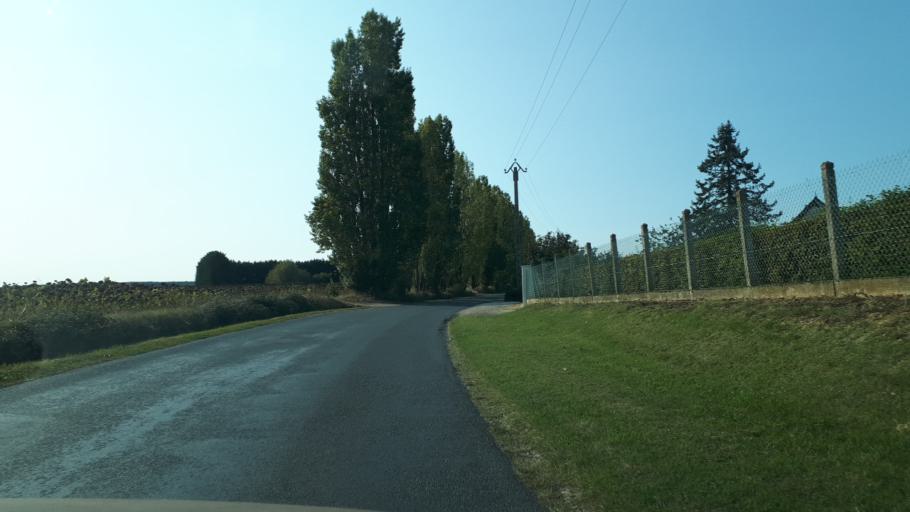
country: FR
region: Centre
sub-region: Departement du Cher
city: Vasselay
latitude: 47.2077
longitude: 2.3998
